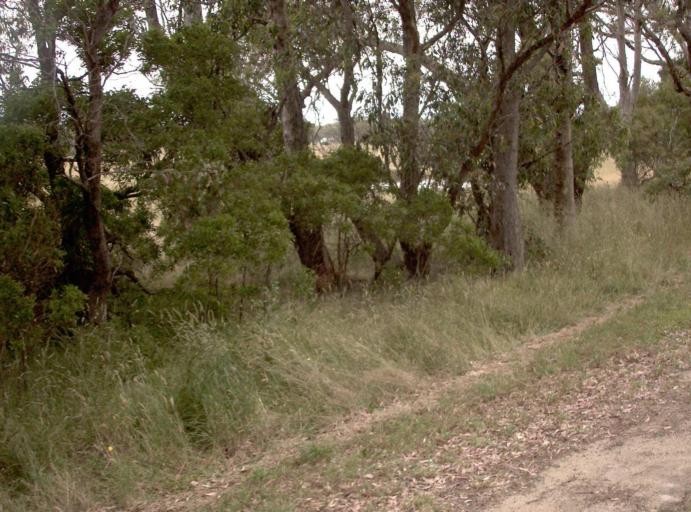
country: AU
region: Victoria
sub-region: Latrobe
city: Traralgon
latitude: -38.5193
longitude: 146.8583
